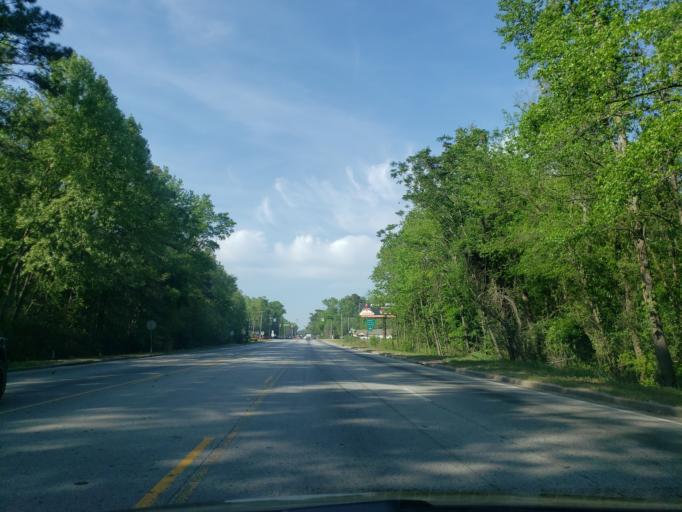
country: US
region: Georgia
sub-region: Chatham County
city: Garden City
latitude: 32.0905
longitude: -81.1970
